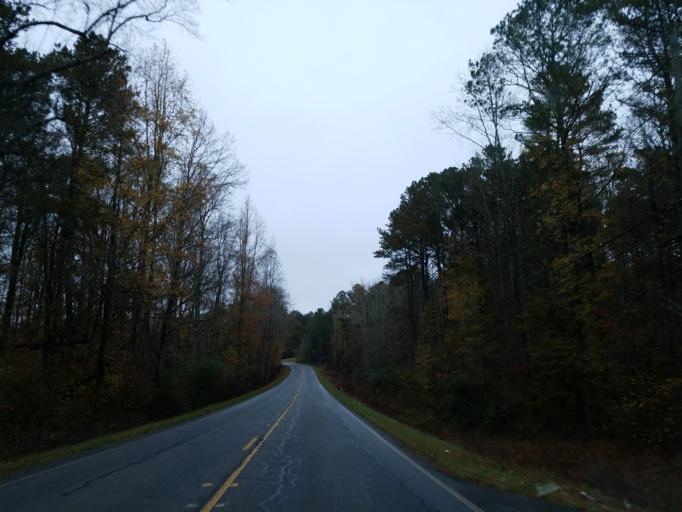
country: US
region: Georgia
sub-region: Cherokee County
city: Ball Ground
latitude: 34.3668
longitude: -84.4813
